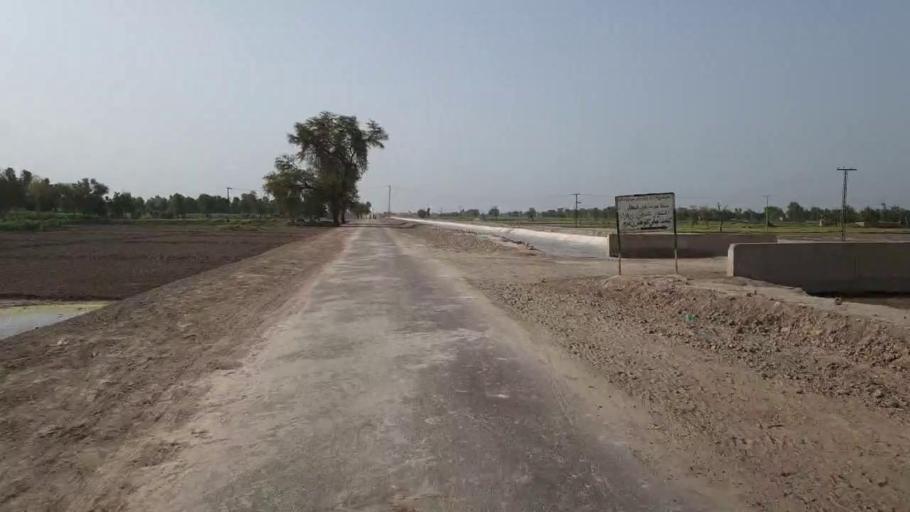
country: PK
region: Sindh
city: Daur
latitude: 26.3311
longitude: 68.1647
